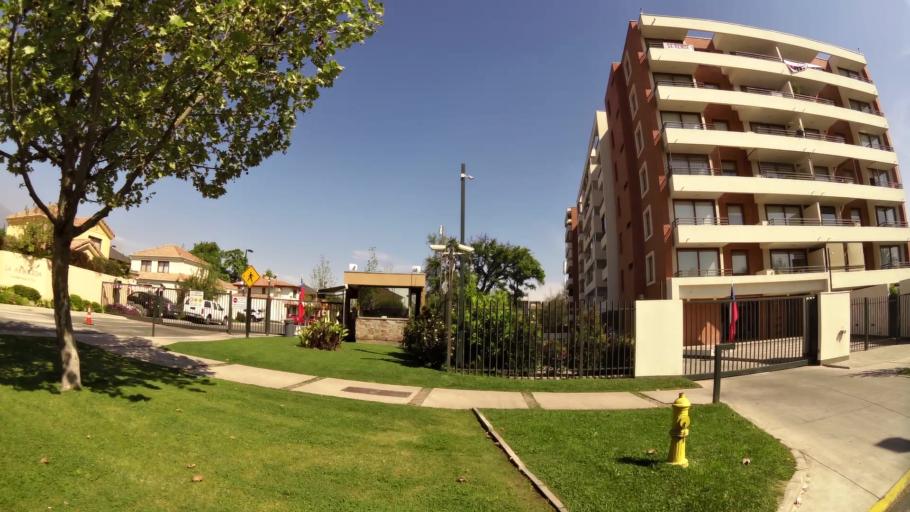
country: CL
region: Santiago Metropolitan
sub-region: Provincia de Santiago
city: Villa Presidente Frei, Nunoa, Santiago, Chile
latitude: -33.4911
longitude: -70.5718
